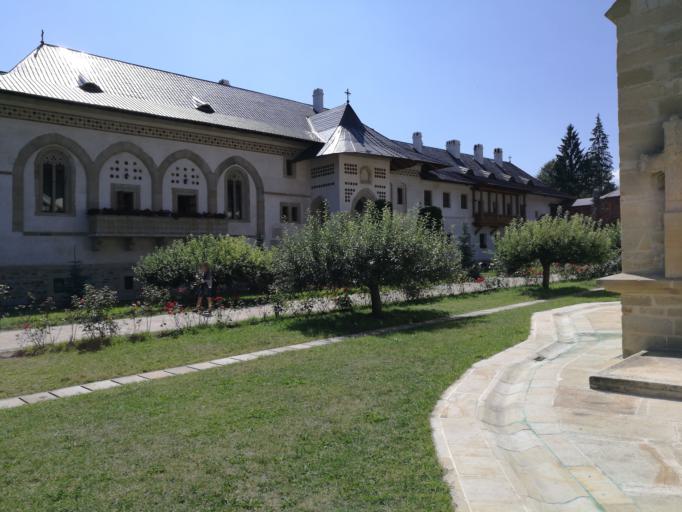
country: RO
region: Suceava
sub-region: Comuna Putna
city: Putna
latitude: 47.8661
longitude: 25.5969
